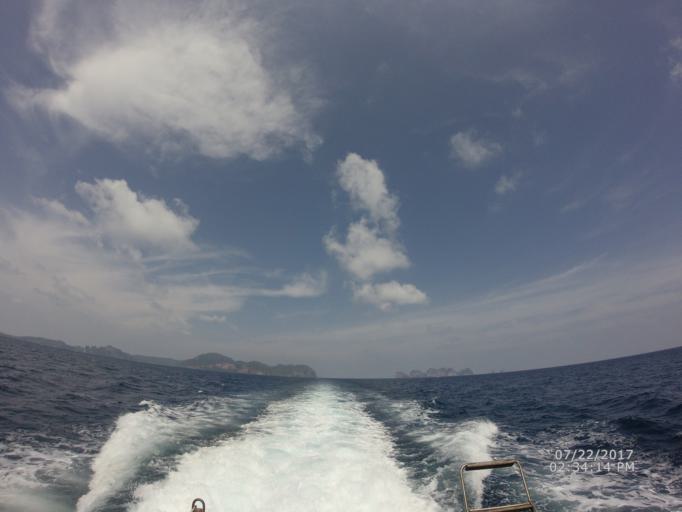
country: TH
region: Phangnga
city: Ban Phru Nai
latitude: 7.7426
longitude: 98.7072
